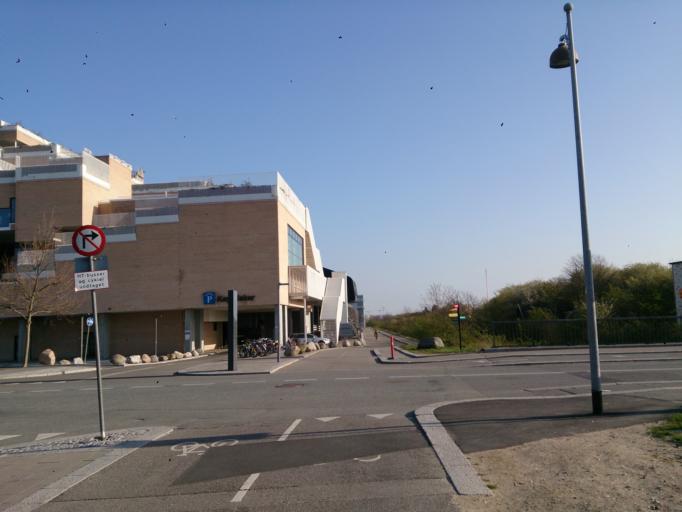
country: DK
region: Capital Region
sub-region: Tarnby Kommune
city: Tarnby
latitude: 55.6303
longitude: 12.5821
